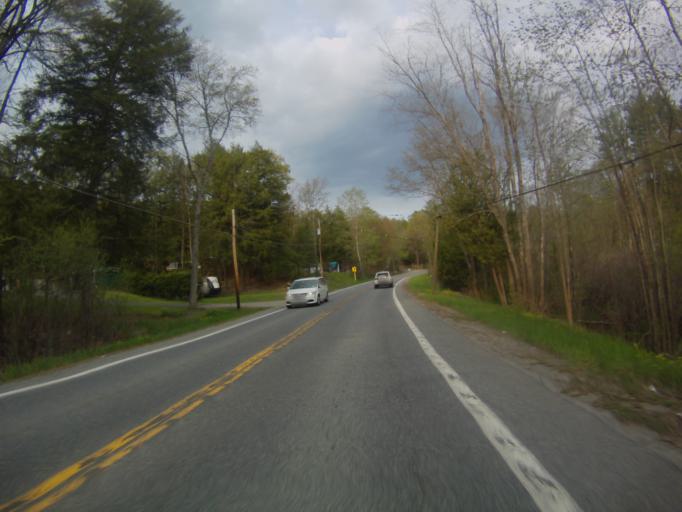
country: US
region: New York
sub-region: Warren County
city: Warrensburg
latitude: 43.6717
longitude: -73.7684
